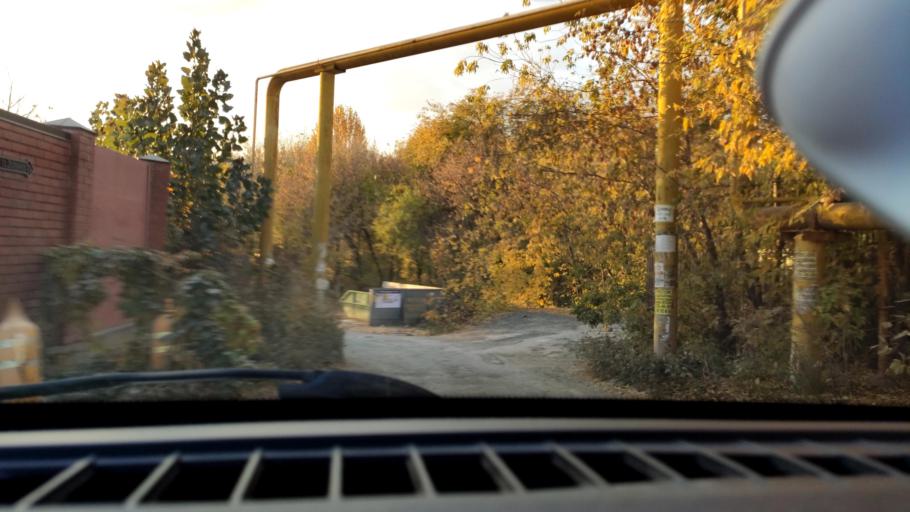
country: RU
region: Samara
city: Samara
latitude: 53.2716
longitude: 50.2297
